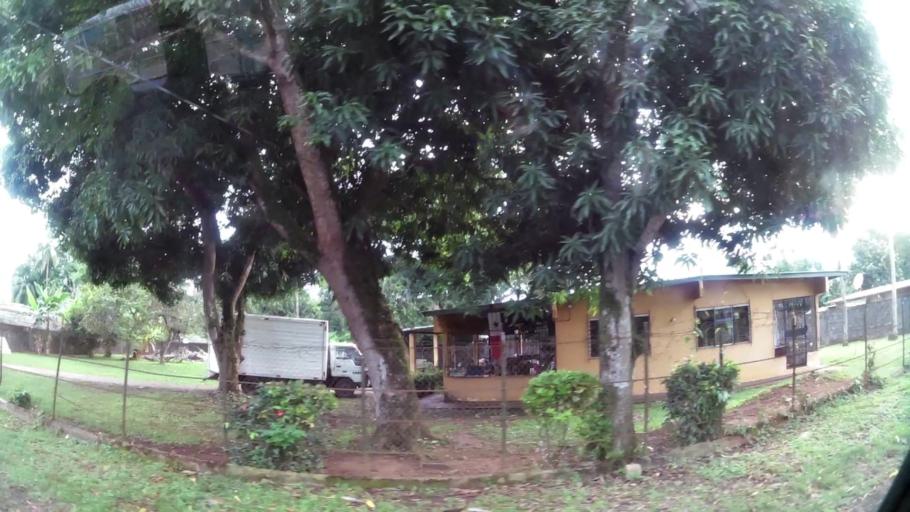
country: PA
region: Panama
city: Tocumen
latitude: 9.0937
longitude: -79.3824
